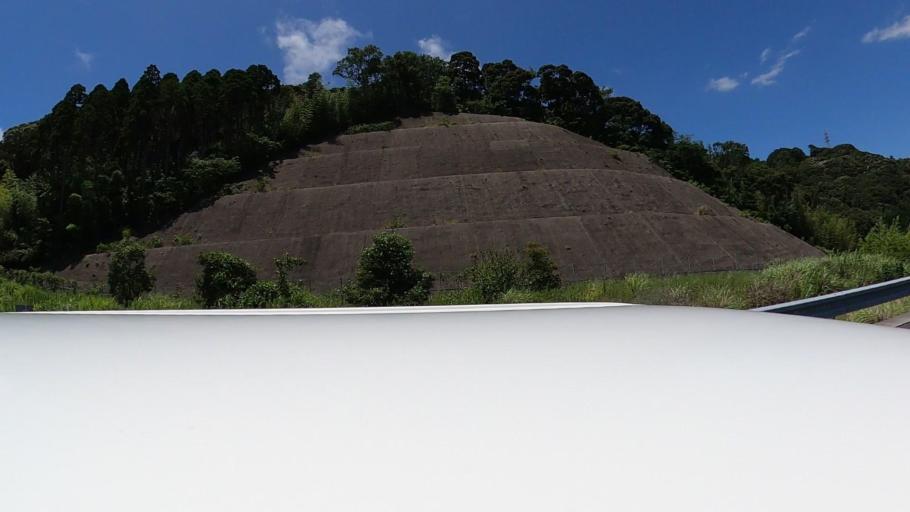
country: JP
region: Miyazaki
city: Nobeoka
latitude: 32.3801
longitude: 131.6199
